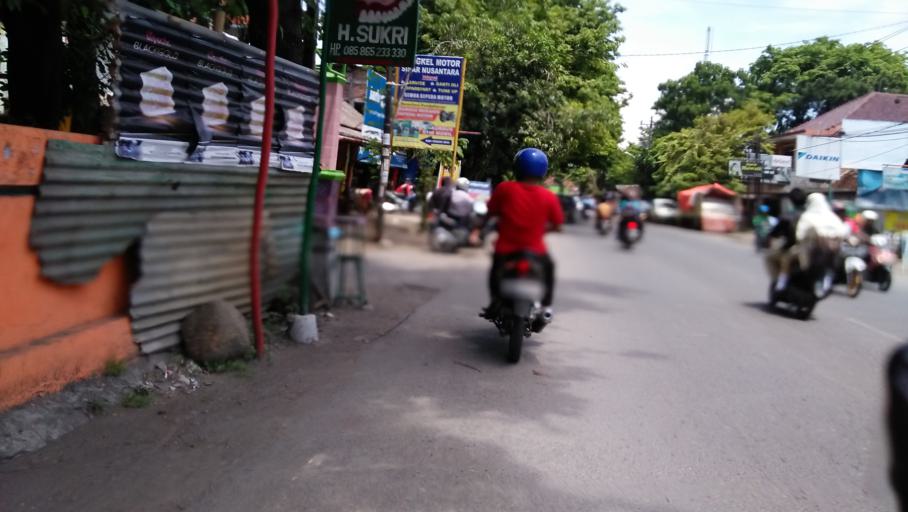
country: ID
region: Central Java
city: Mranggen
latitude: -7.0181
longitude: 110.4715
